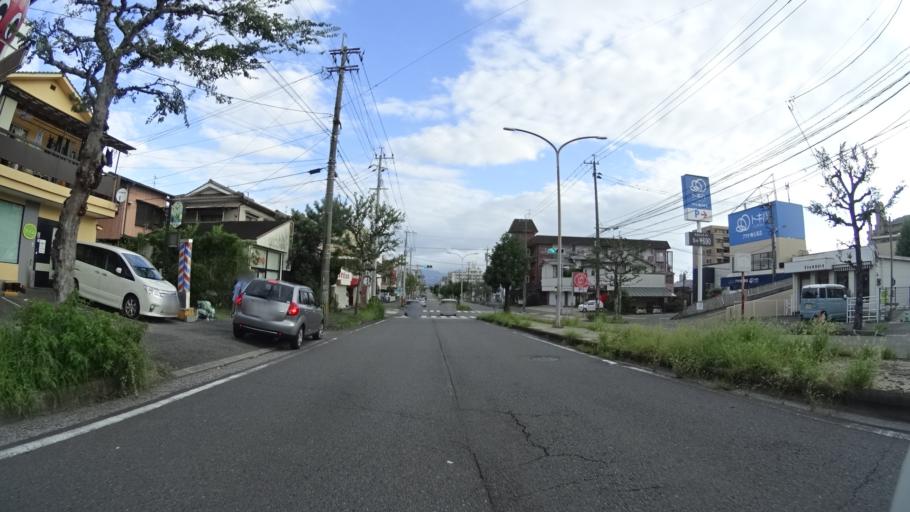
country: JP
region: Oita
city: Beppu
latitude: 33.2888
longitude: 131.4962
